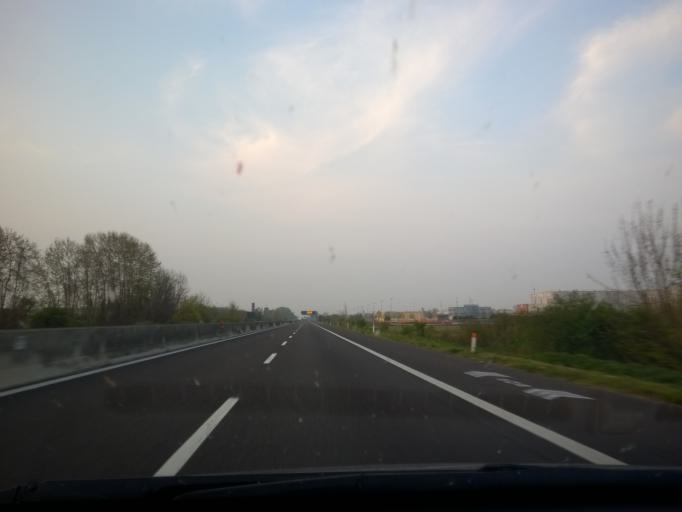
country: IT
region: Veneto
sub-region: Provincia di Padova
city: Villatora
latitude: 45.3719
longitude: 11.9499
